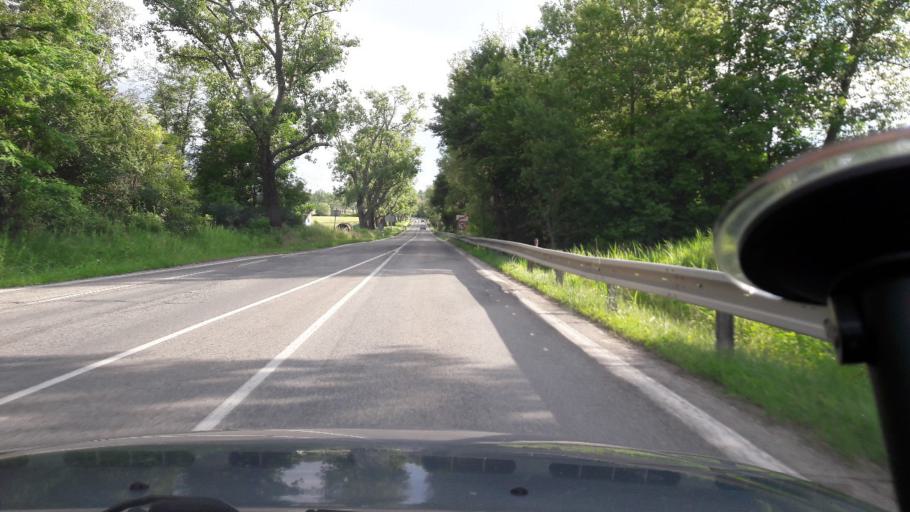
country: SK
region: Bratislavsky
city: Modra
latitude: 48.3252
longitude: 17.3021
